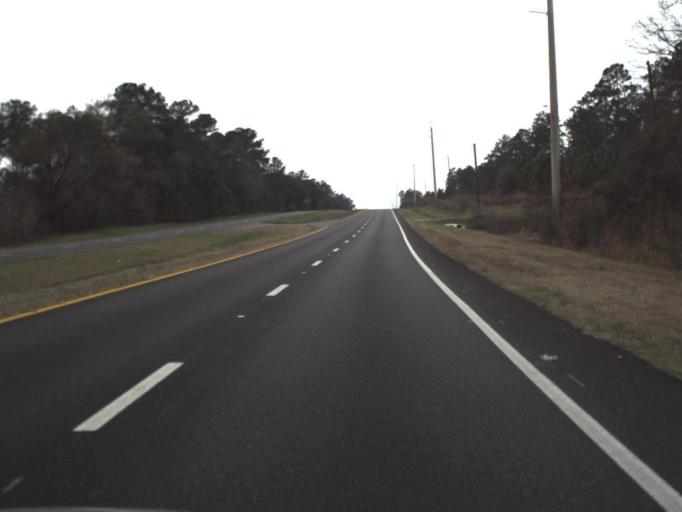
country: US
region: Florida
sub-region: Jefferson County
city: Monticello
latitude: 30.4112
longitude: -83.9241
